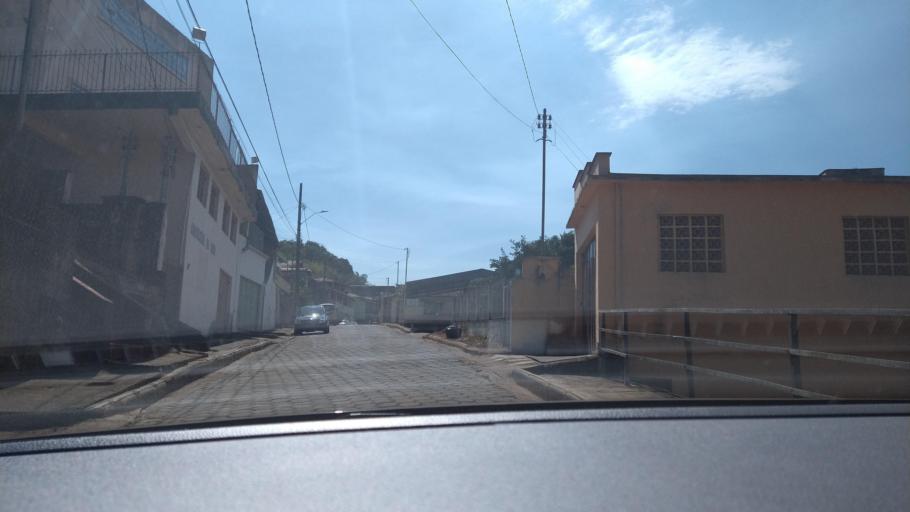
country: BR
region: Minas Gerais
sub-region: Rio Piracicaba
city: Rio Piracicaba
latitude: -19.9359
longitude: -43.1764
